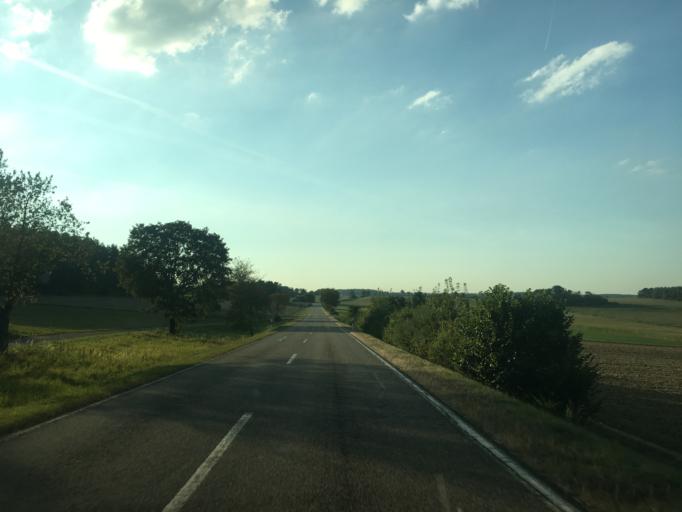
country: DE
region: Baden-Wuerttemberg
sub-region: Tuebingen Region
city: Hayingen
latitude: 48.2644
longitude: 9.4979
